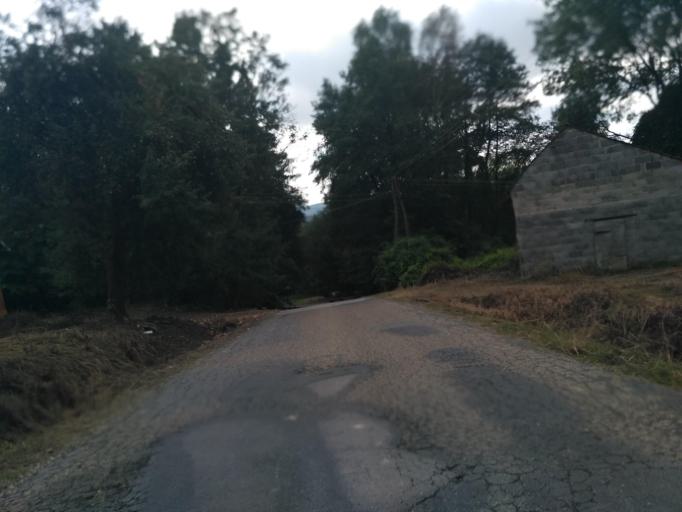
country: PL
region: Subcarpathian Voivodeship
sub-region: Powiat ropczycko-sedziszowski
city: Niedzwiada
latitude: 49.9423
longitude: 21.4620
